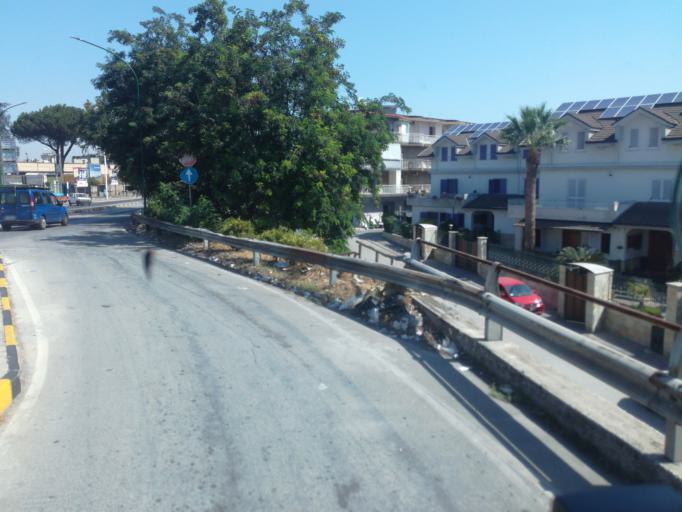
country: IT
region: Campania
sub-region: Provincia di Napoli
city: Arpino
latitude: 40.8843
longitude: 14.3200
